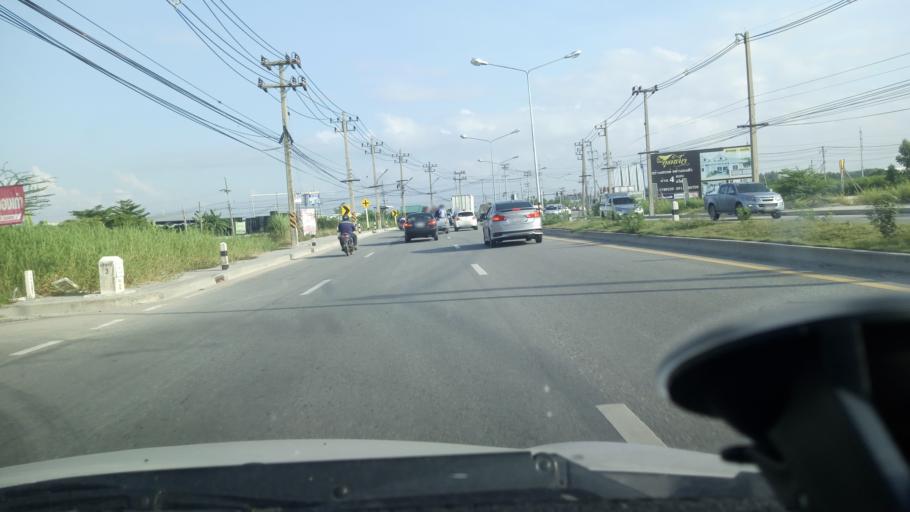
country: TH
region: Chon Buri
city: Phan Thong
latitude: 13.4418
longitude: 101.1047
